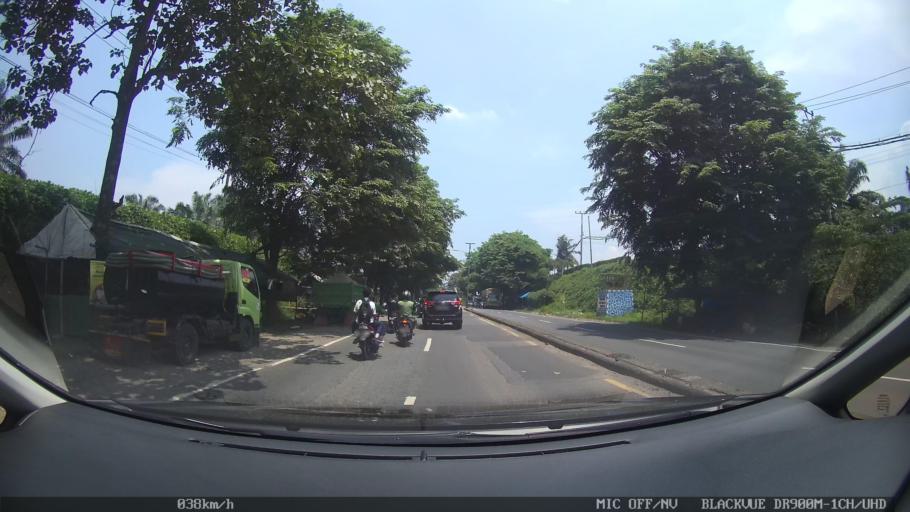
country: ID
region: Lampung
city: Natar
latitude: -5.3327
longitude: 105.2091
